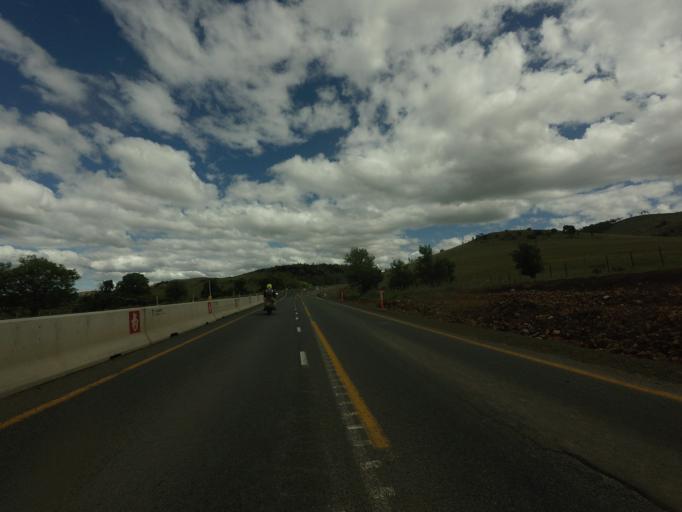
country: AU
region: Tasmania
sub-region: Brighton
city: Bridgewater
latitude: -42.2180
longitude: 147.4101
